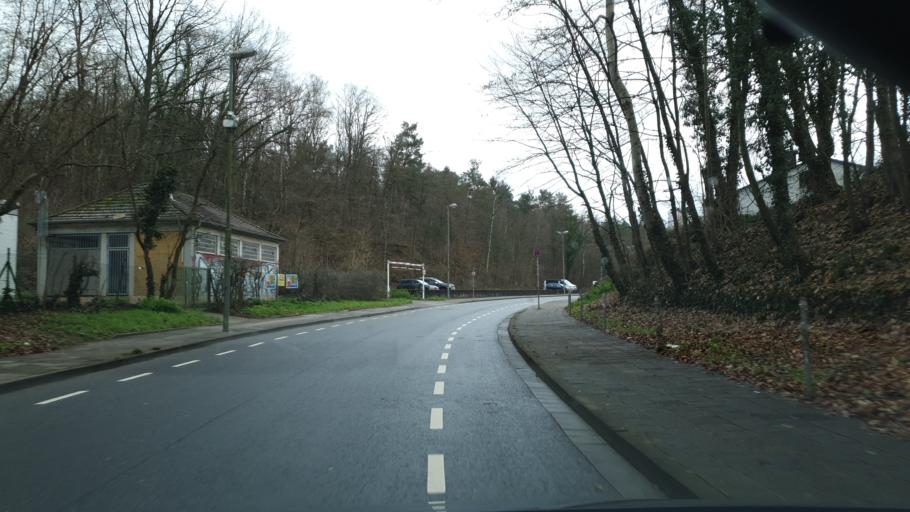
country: DE
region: Rheinland-Pfalz
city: Kaiserslautern
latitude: 49.4369
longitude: 7.7824
